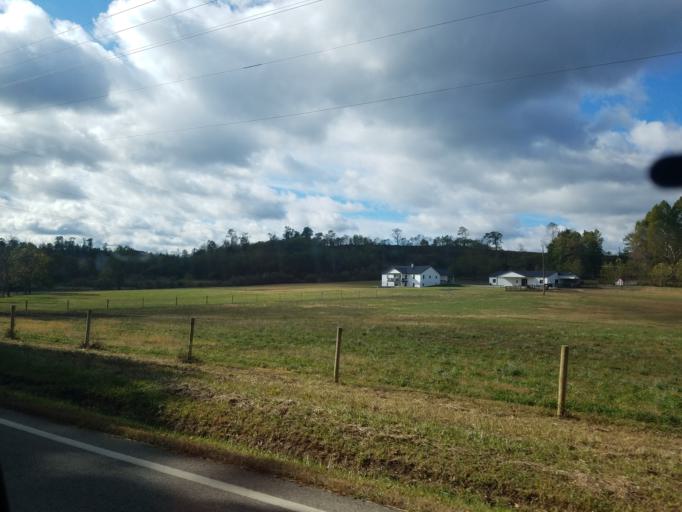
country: US
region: Ohio
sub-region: Vinton County
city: McArthur
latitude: 39.1933
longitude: -82.4770
